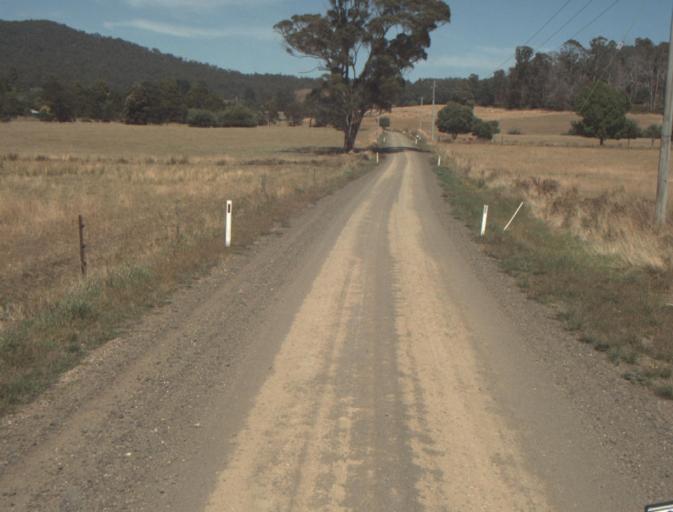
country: AU
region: Tasmania
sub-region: Launceston
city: Mayfield
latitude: -41.2529
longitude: 147.1336
